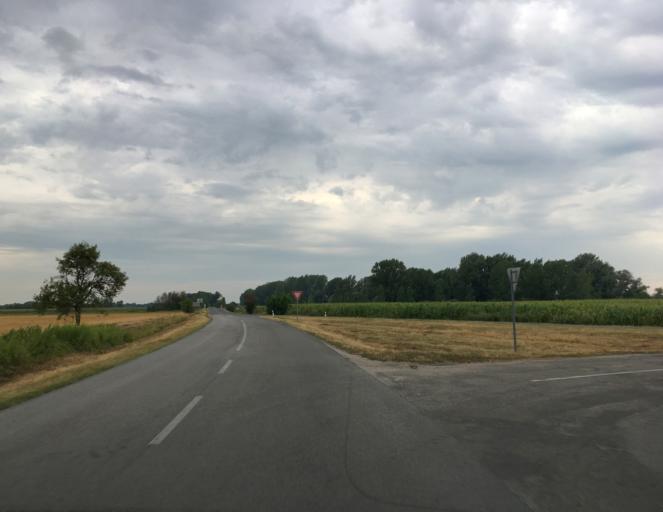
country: SK
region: Trnavsky
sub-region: Okres Dunajska Streda
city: Velky Meder
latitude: 47.9088
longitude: 17.6834
